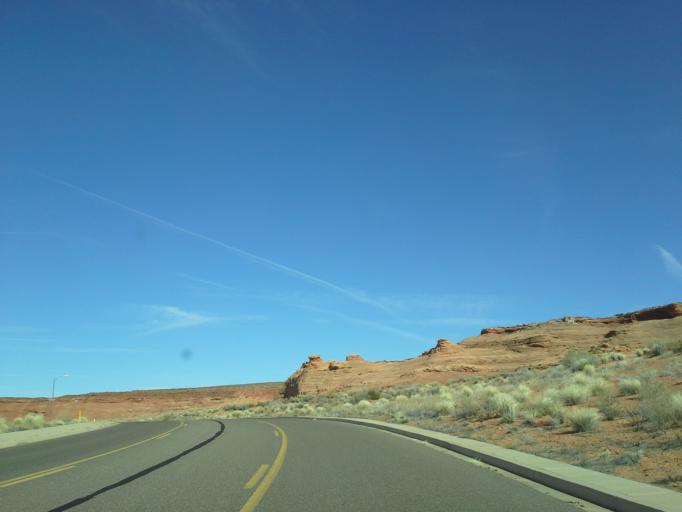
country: US
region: Arizona
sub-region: Coconino County
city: Page
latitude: 36.9314
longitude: -111.4698
